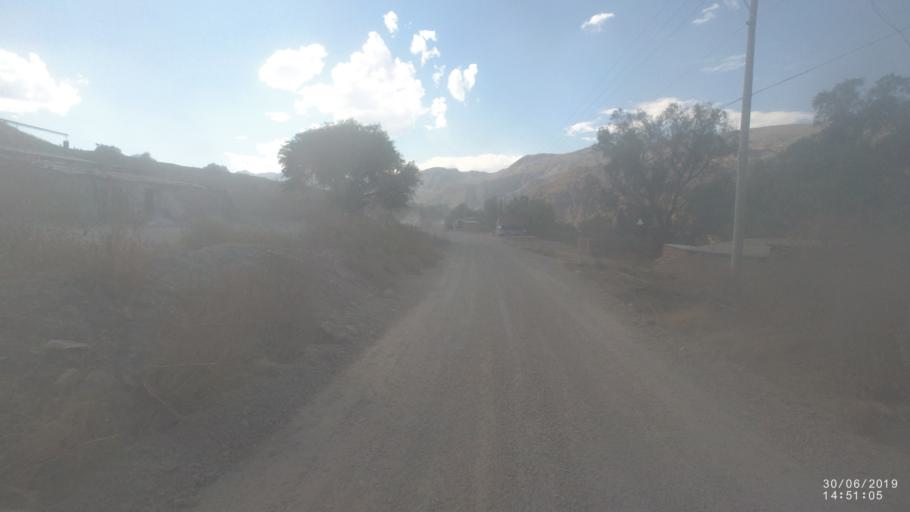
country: BO
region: Cochabamba
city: Irpa Irpa
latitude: -17.7739
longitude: -66.3438
